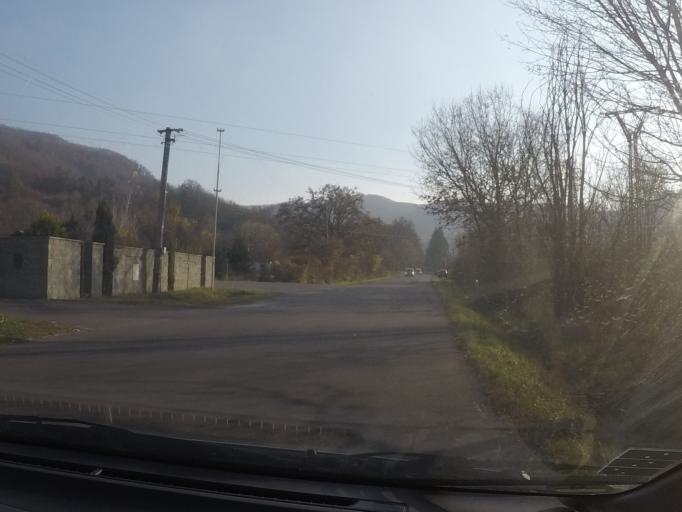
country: SK
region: Banskobystricky
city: Zarnovica
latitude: 48.4710
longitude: 18.7247
